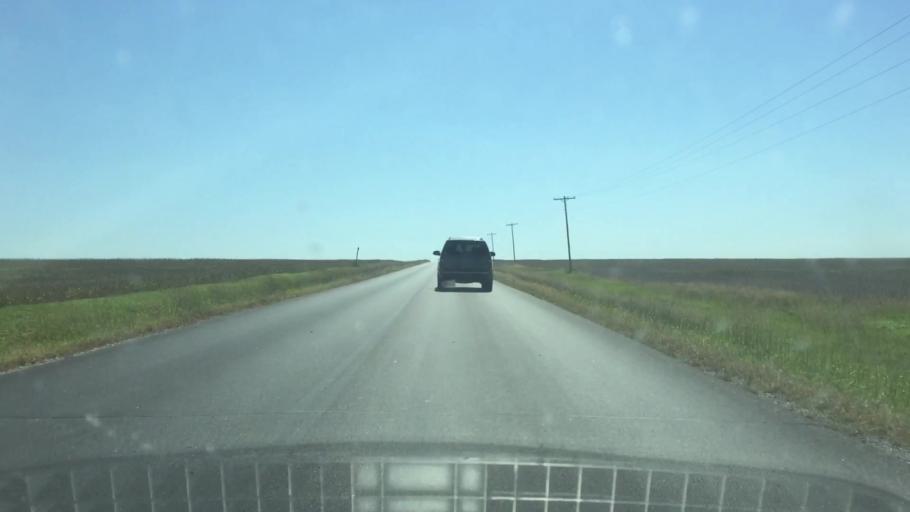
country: US
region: Kansas
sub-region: Marshall County
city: Marysville
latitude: 39.8701
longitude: -96.6009
